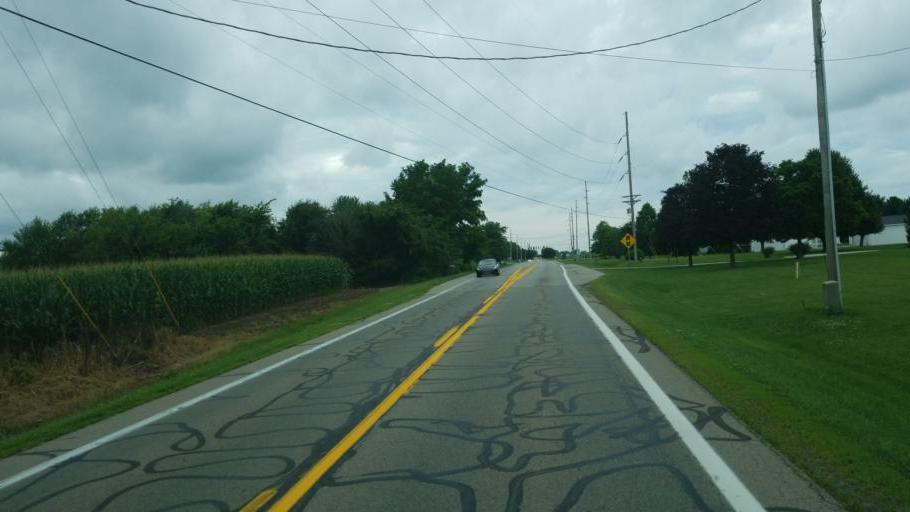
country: US
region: Ohio
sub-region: Pickaway County
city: Commercial Point
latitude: 39.7671
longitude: -83.0255
